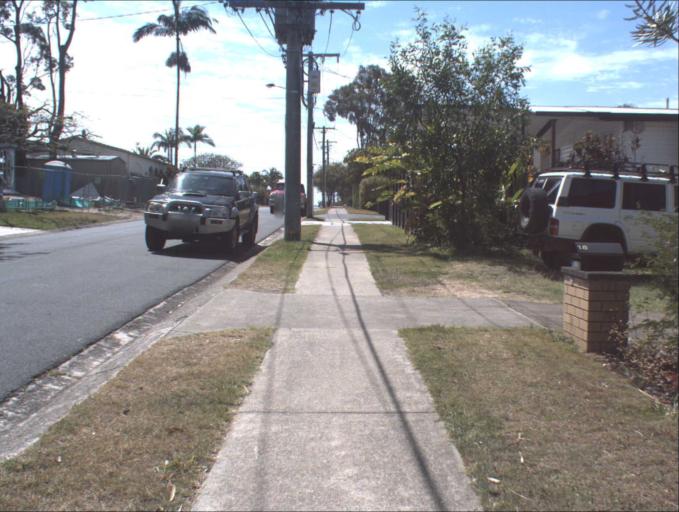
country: AU
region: Queensland
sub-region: Logan
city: Rochedale South
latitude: -27.5952
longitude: 153.1261
